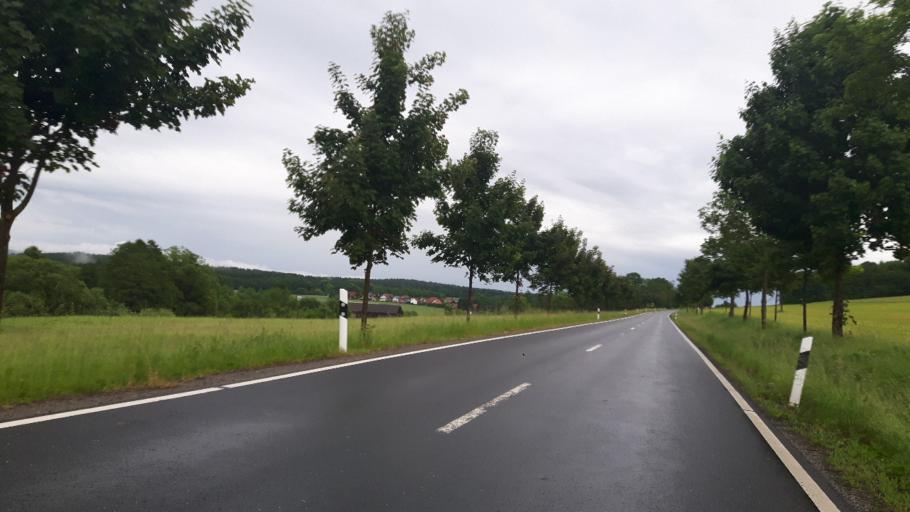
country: DE
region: Thuringia
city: Bockstadt
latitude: 50.4073
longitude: 10.8685
